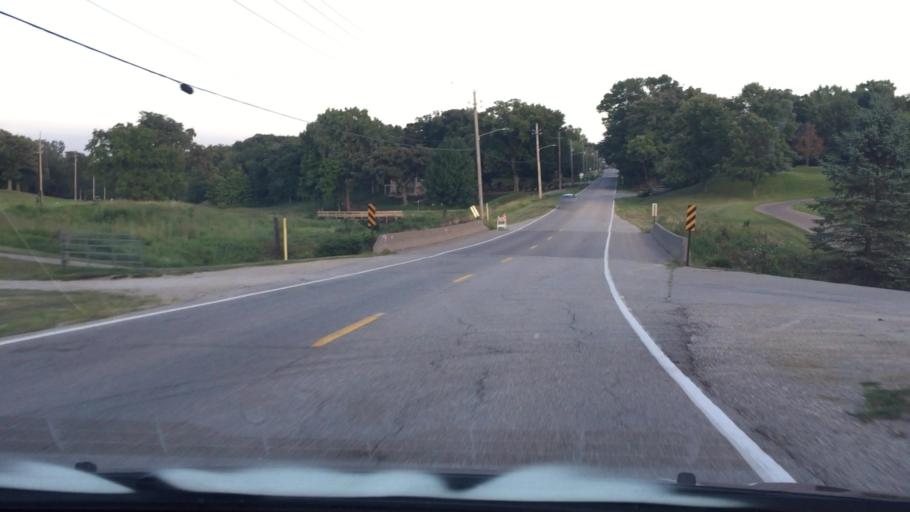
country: US
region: Iowa
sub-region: Muscatine County
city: Muscatine
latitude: 41.4495
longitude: -91.0557
